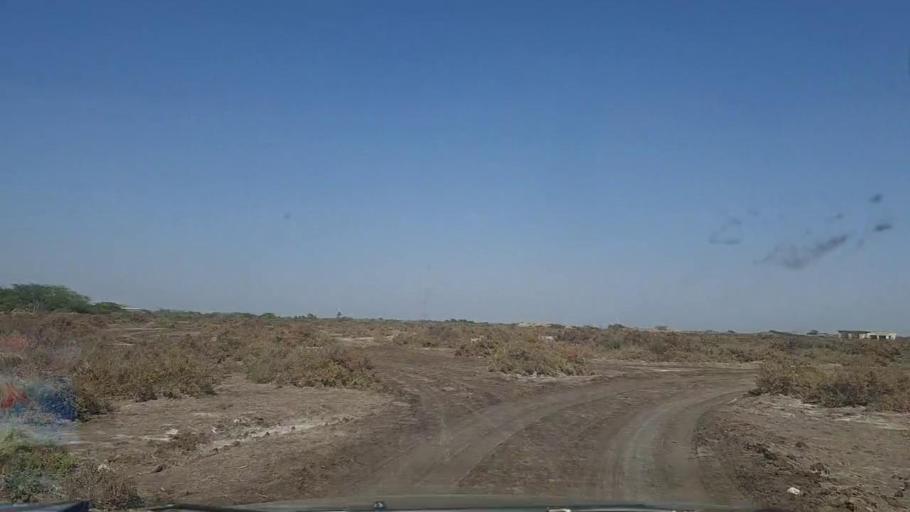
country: PK
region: Sindh
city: Chuhar Jamali
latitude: 24.2732
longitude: 67.7562
